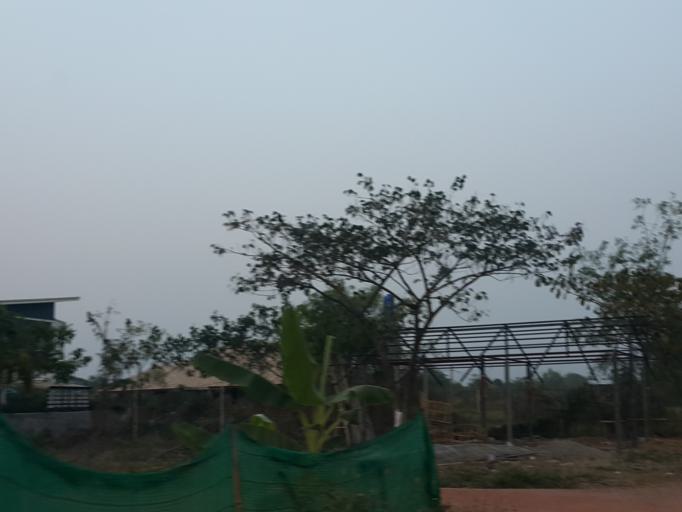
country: TH
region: Chiang Mai
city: San Kamphaeng
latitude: 18.7760
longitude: 99.0759
